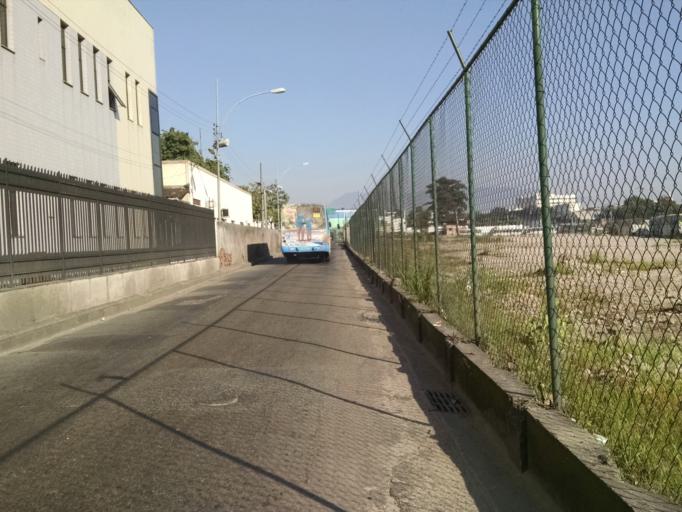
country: BR
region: Rio de Janeiro
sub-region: Sao Joao De Meriti
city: Sao Joao de Meriti
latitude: -22.8048
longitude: -43.3622
